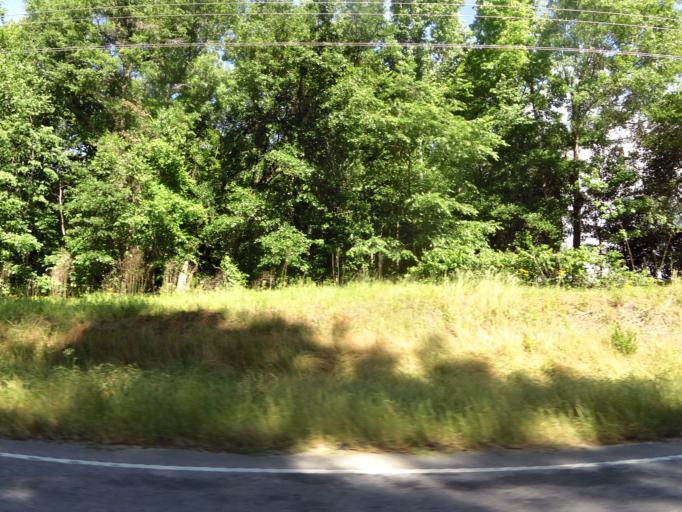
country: US
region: South Carolina
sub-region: Bamberg County
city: Denmark
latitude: 33.2791
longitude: -81.1516
